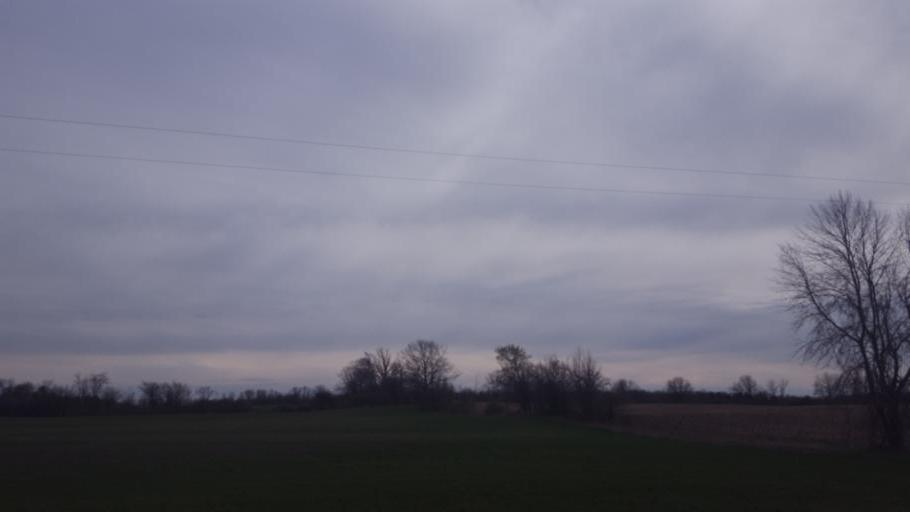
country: US
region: Michigan
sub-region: Clare County
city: Clare
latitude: 43.8731
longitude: -84.6683
